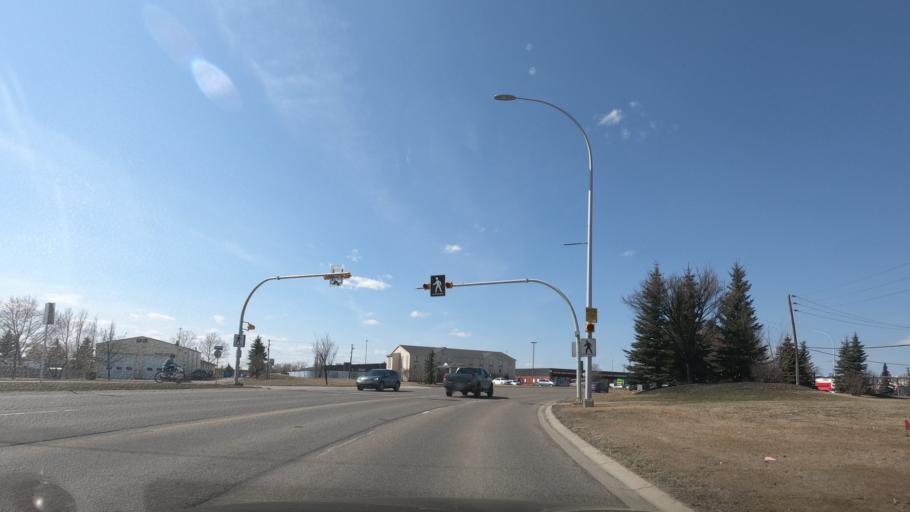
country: CA
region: Alberta
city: Airdrie
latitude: 51.2839
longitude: -113.9953
